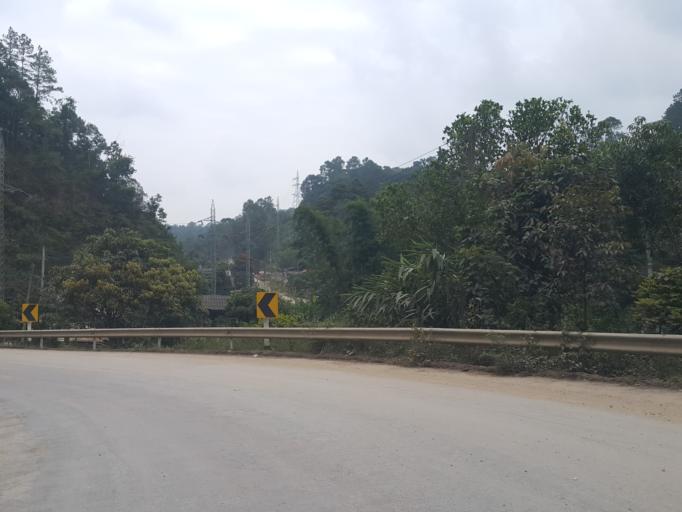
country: TH
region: Mae Hong Son
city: Mae Hi
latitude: 19.2458
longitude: 98.6532
